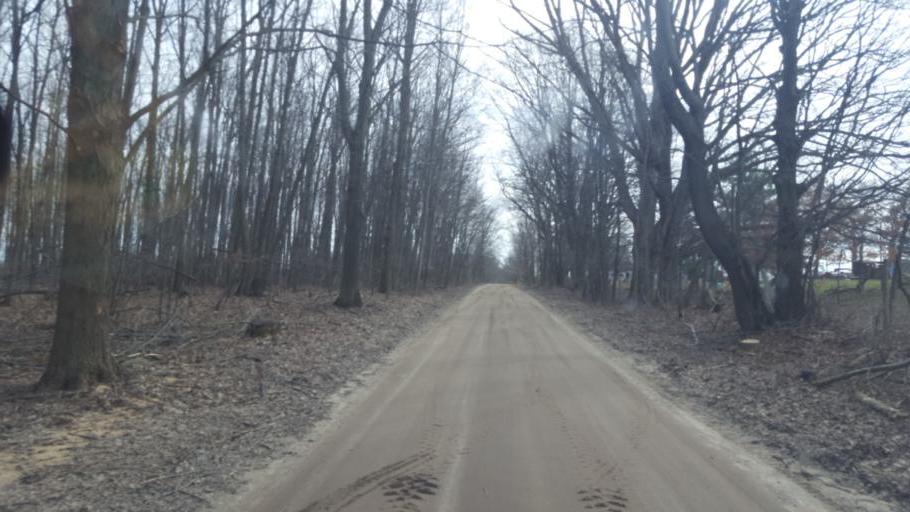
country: US
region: Michigan
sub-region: Isabella County
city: Lake Isabella
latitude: 43.6650
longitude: -85.1264
